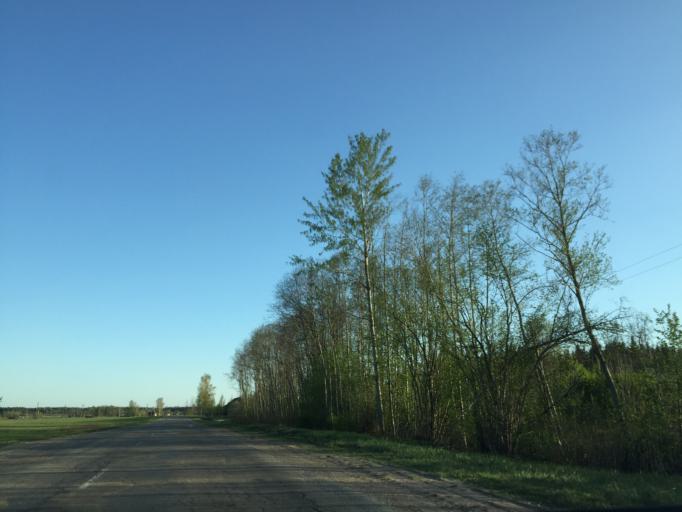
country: LV
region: Koknese
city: Koknese
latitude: 56.6906
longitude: 25.4870
